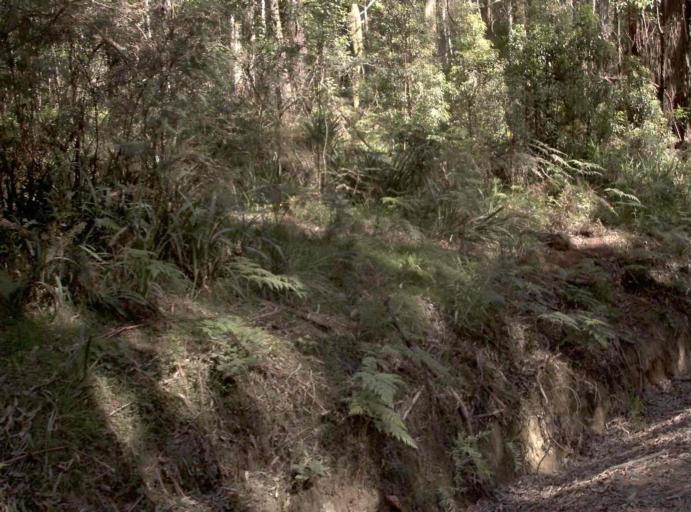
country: AU
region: New South Wales
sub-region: Bombala
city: Bombala
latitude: -37.2440
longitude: 148.7574
